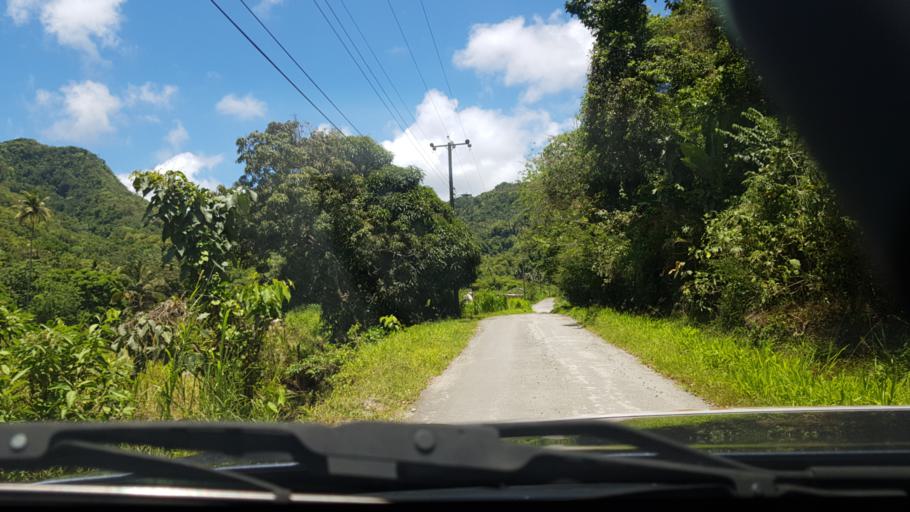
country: LC
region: Anse-la-Raye
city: Canaries
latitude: 13.9009
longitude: -61.0617
